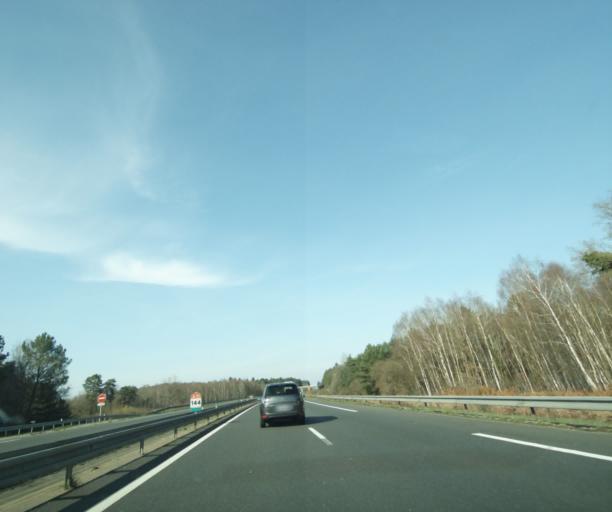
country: FR
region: Centre
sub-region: Departement du Loir-et-Cher
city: Nouan-le-Fuzelier
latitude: 47.5298
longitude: 2.0036
